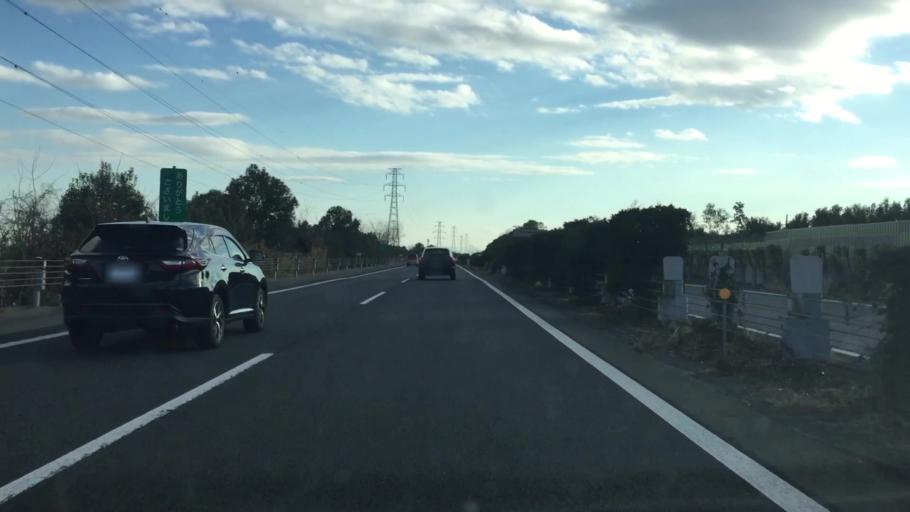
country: JP
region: Gunma
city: Shibukawa
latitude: 36.4581
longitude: 139.0128
